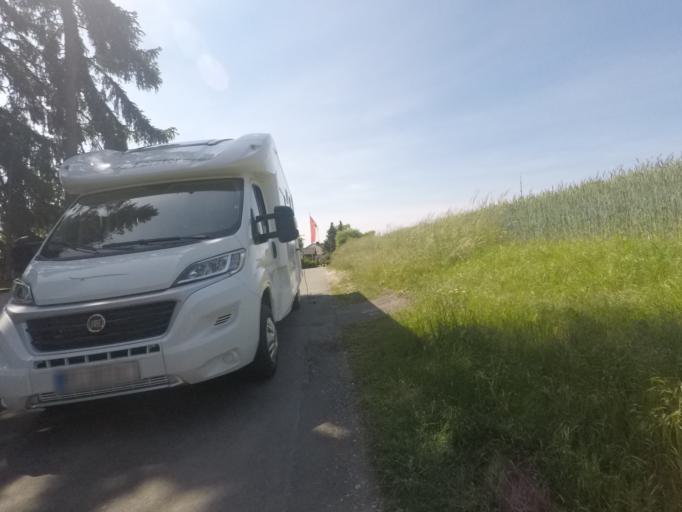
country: DE
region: North Rhine-Westphalia
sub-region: Regierungsbezirk Detmold
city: Bielefeld
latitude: 52.0035
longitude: 8.4941
